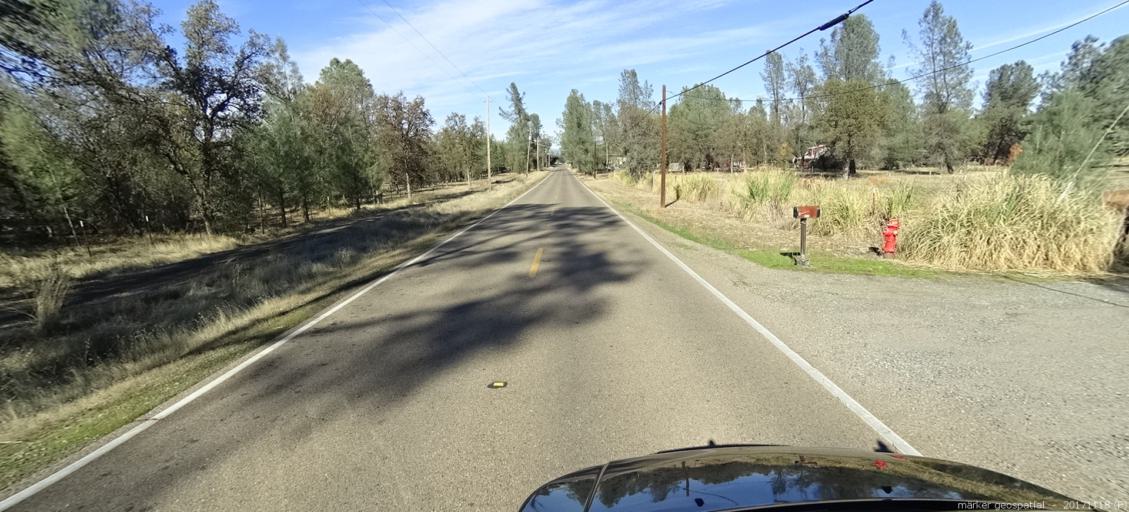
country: US
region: California
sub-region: Shasta County
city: Redding
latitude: 40.4676
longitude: -122.4546
